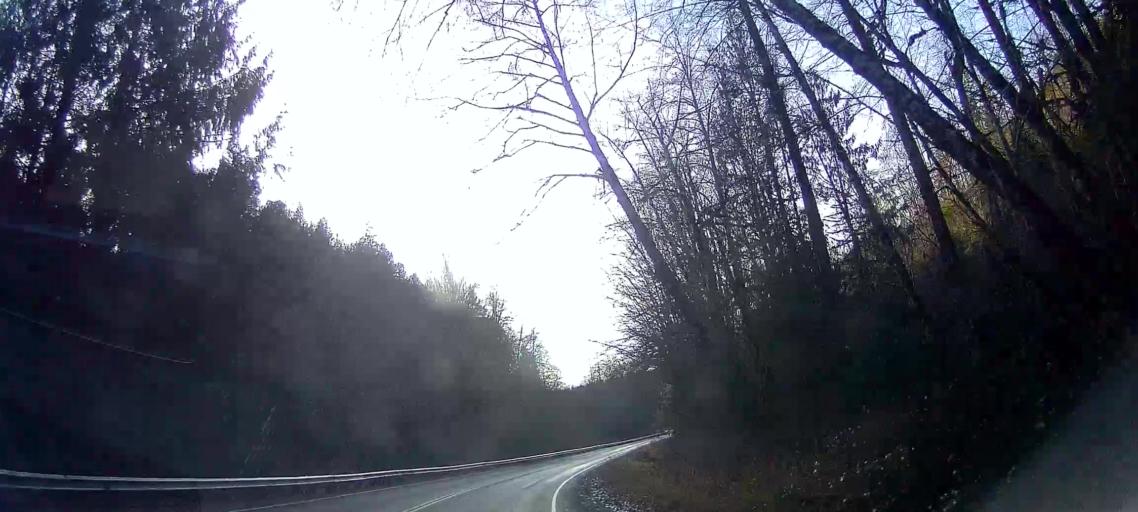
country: US
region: Washington
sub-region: Skagit County
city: Sedro-Woolley
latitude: 48.5484
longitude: -121.8722
